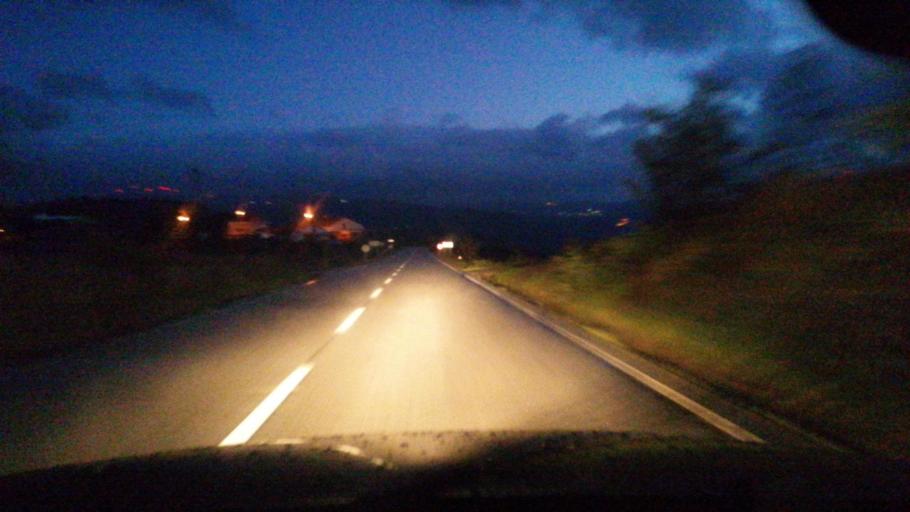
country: PT
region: Viseu
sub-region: Tabuaco
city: Tabuaco
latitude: 41.1269
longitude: -7.5170
